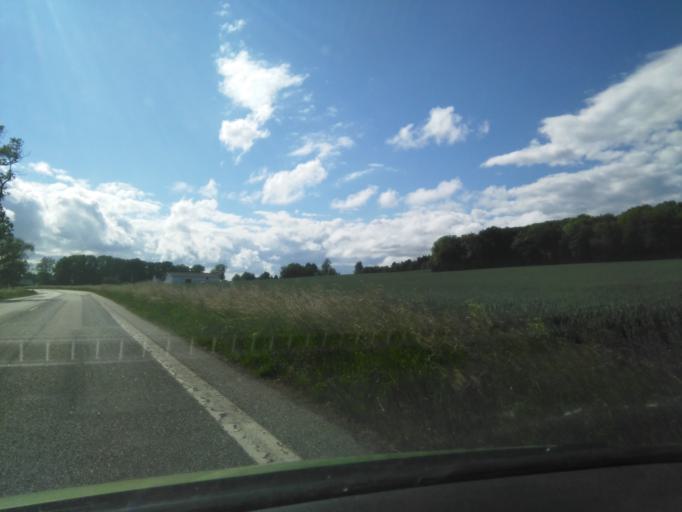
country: DK
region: Capital Region
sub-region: Bornholm Kommune
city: Nexo
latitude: 55.0634
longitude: 15.0852
